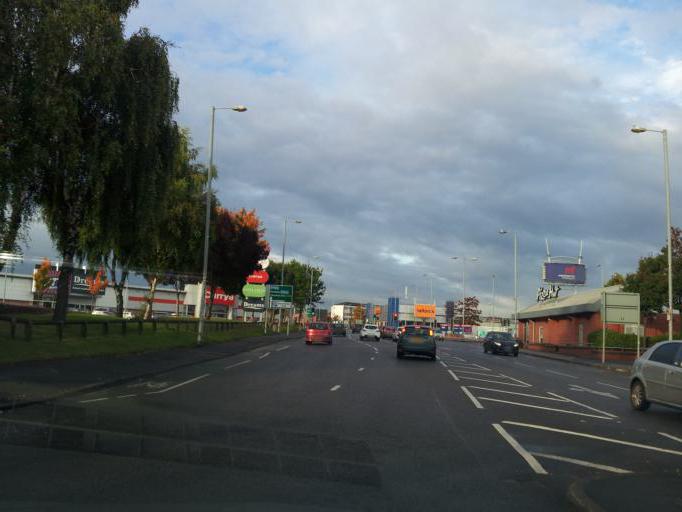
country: GB
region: England
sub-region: Manchester
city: Cheetham Hill
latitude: 53.4979
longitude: -2.2371
